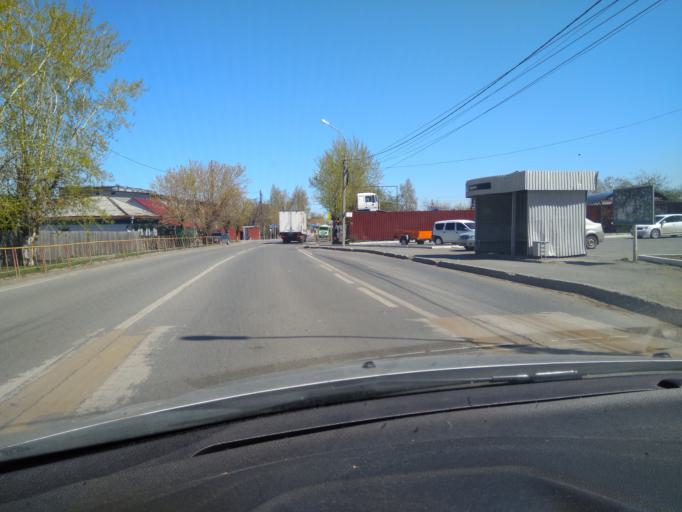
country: RU
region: Tjumen
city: Moskovskiy
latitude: 57.1571
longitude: 65.4500
